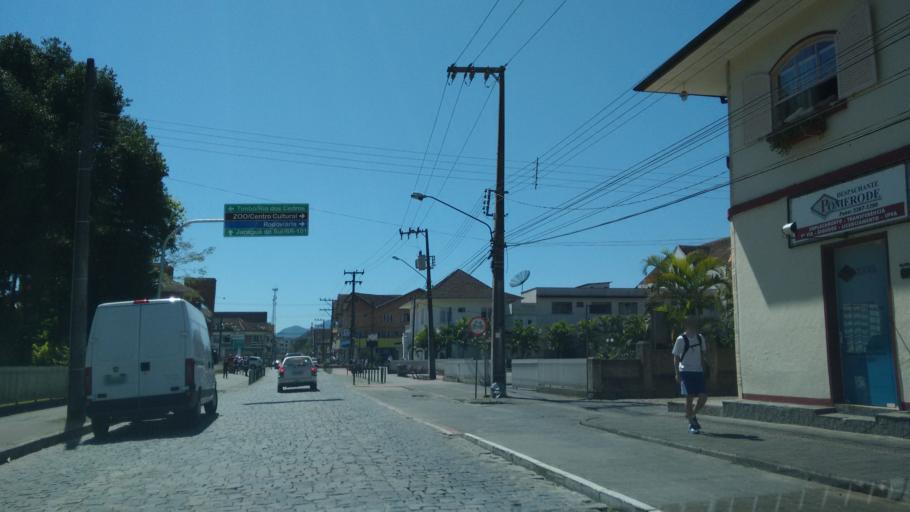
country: BR
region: Santa Catarina
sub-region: Pomerode
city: Pomerode
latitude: -26.7383
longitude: -49.1765
